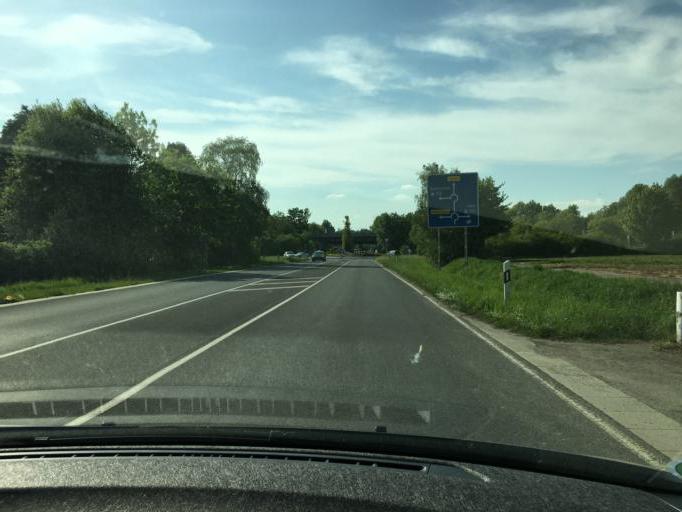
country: DE
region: North Rhine-Westphalia
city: Bruhl
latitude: 50.8028
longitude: 6.9086
